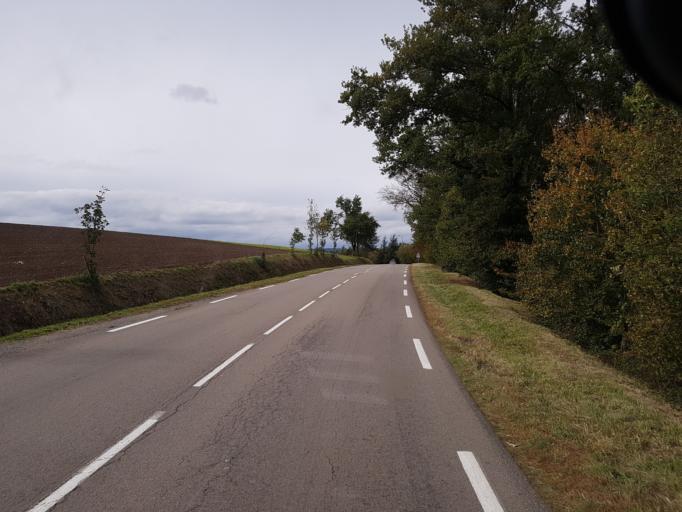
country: FR
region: Rhone-Alpes
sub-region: Departement de la Loire
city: La Ricamarie
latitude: 45.4149
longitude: 4.2998
